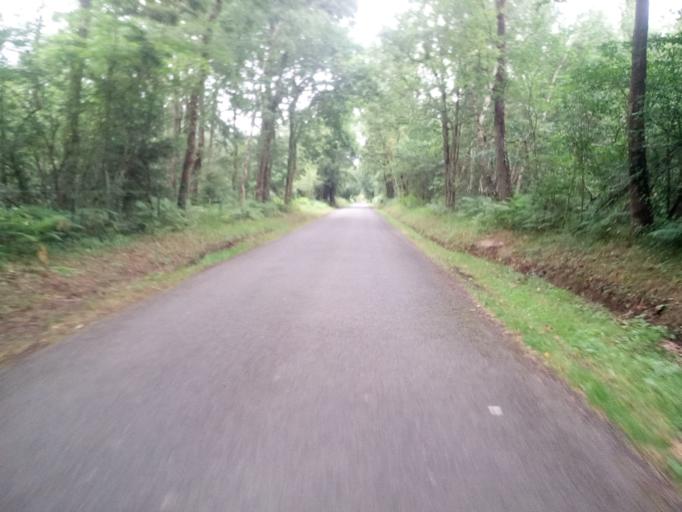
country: FR
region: Lower Normandy
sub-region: Departement du Calvados
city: Clinchamps-sur-Orne
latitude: 49.0283
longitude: -0.3953
